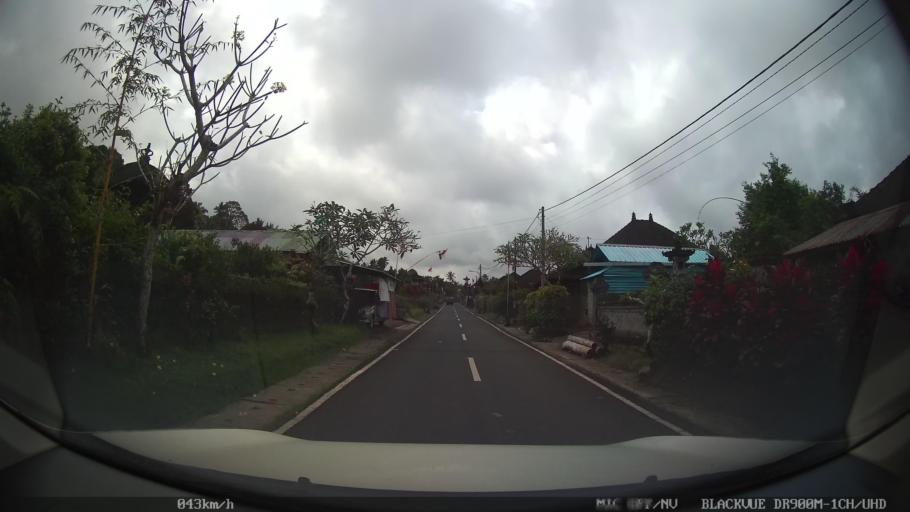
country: ID
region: Bali
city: Pemijian
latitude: -8.4499
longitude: 115.2286
